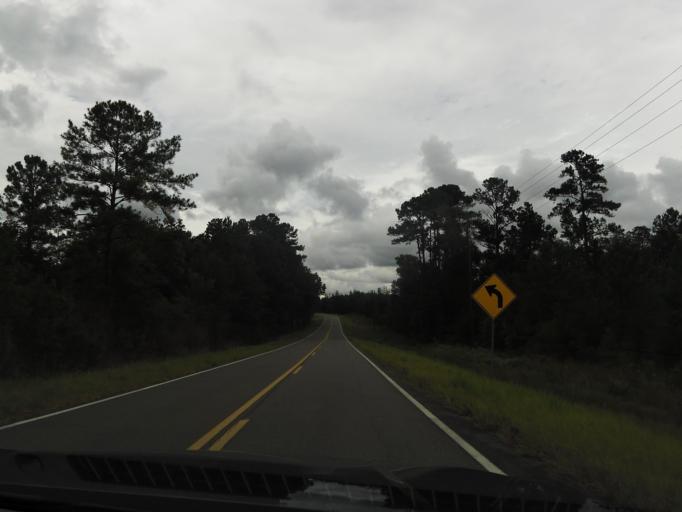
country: US
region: Florida
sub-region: Baker County
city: Macclenny
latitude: 30.4406
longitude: -82.1982
